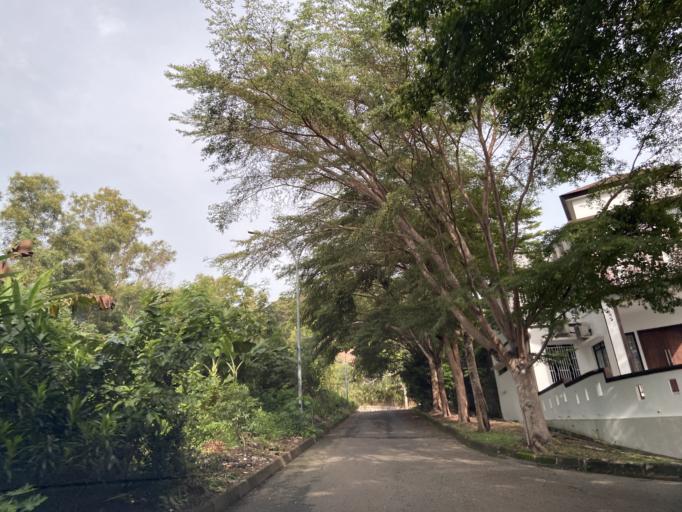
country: SG
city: Singapore
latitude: 1.0991
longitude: 104.0296
